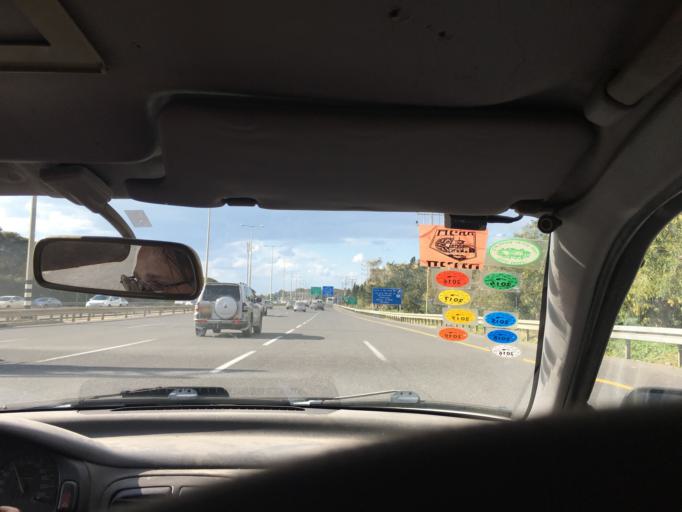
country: IL
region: Tel Aviv
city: Ramat HaSharon
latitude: 32.1372
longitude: 34.8279
